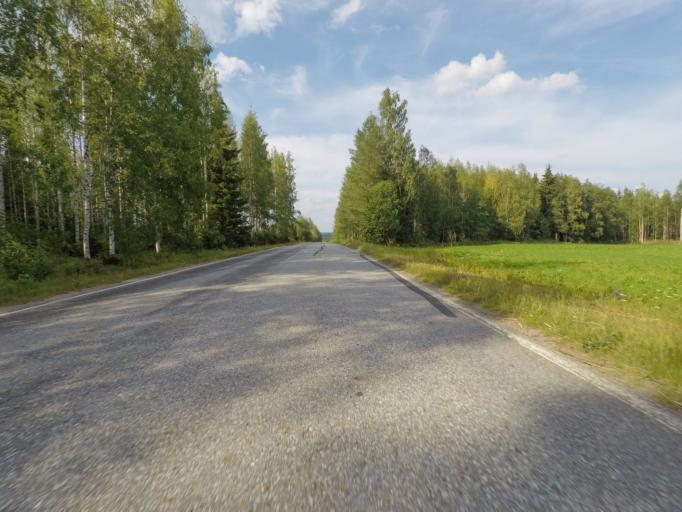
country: FI
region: Southern Savonia
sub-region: Savonlinna
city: Sulkava
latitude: 61.7077
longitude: 28.2105
